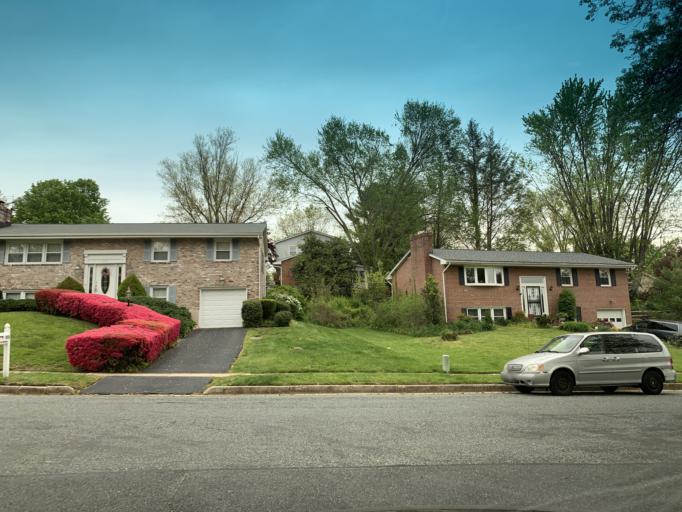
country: US
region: Maryland
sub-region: Harford County
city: South Bel Air
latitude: 39.5306
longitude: -76.3372
